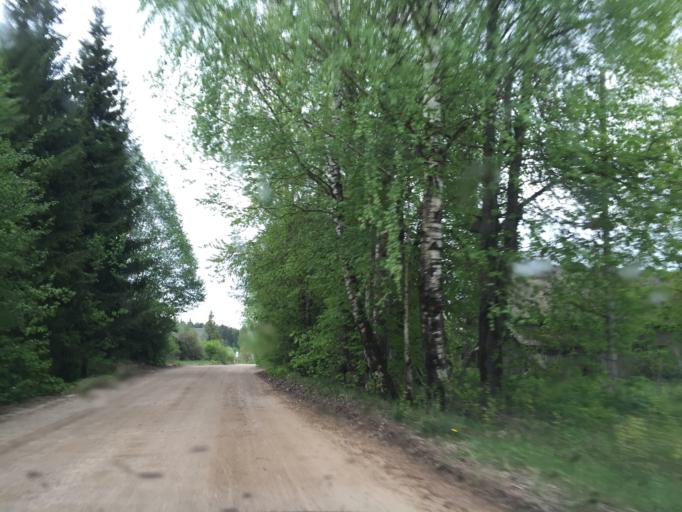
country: LV
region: Ogre
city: Ogre
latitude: 56.8253
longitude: 24.6526
